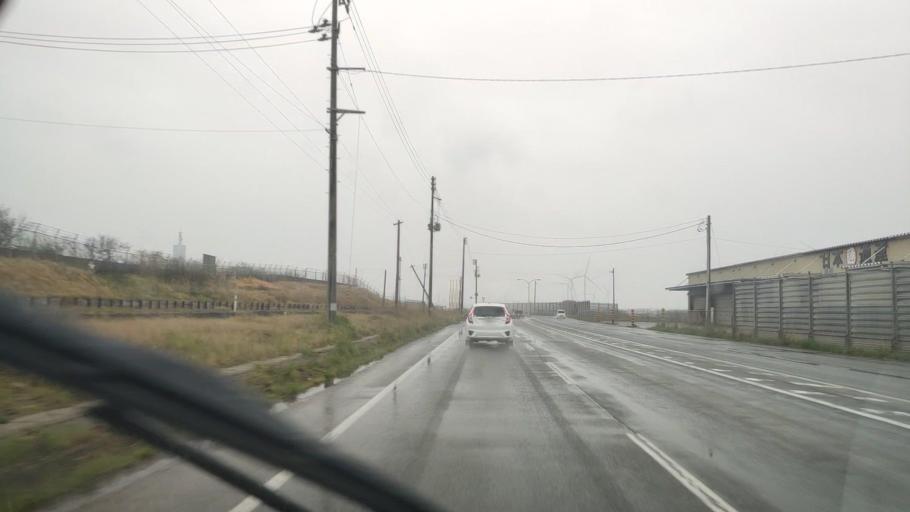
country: JP
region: Akita
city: Akita Shi
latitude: 39.7630
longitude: 140.0510
